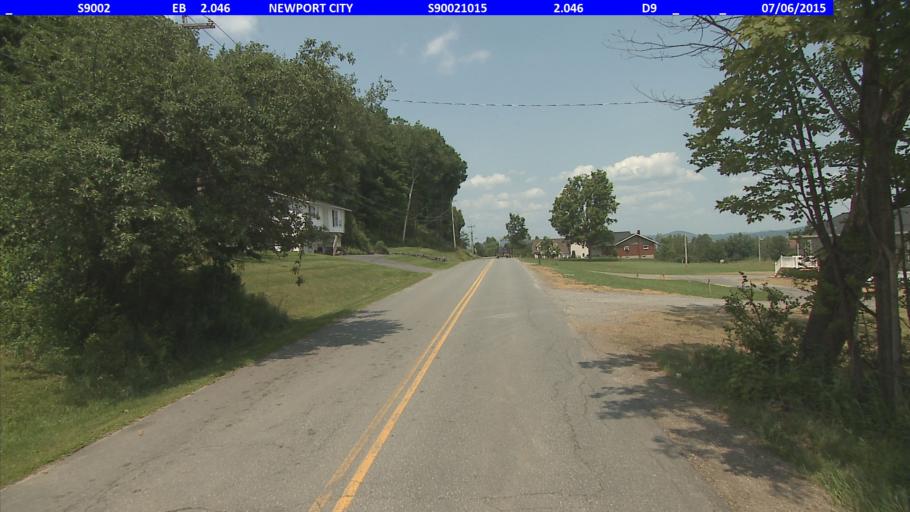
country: US
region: Vermont
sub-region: Orleans County
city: Newport
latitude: 44.9441
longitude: -72.2372
